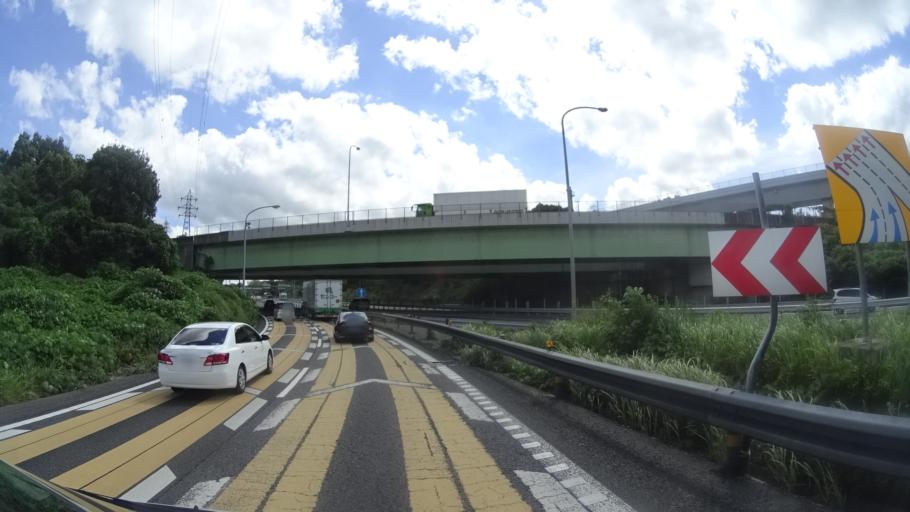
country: JP
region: Shiga Prefecture
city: Kusatsu
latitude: 34.9700
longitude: 135.9270
